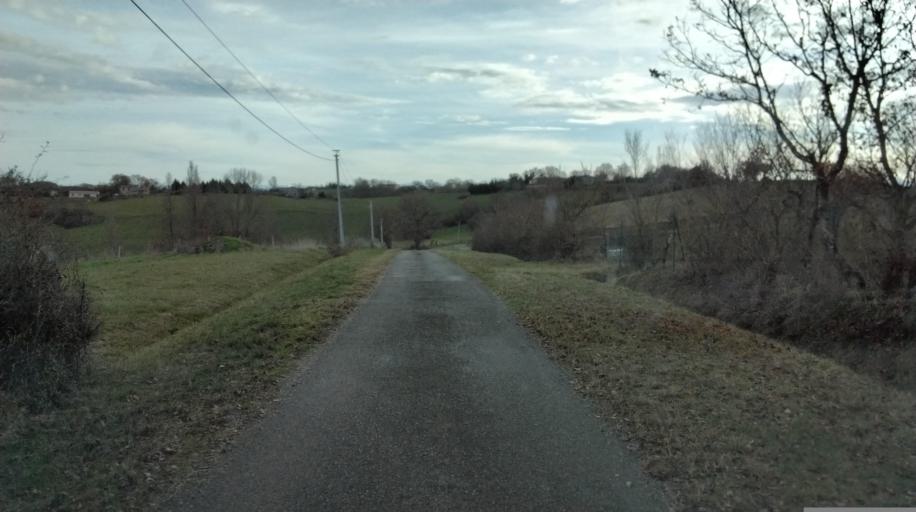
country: FR
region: Midi-Pyrenees
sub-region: Departement de la Haute-Garonne
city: Le Fousseret
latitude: 43.3047
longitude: 0.9820
